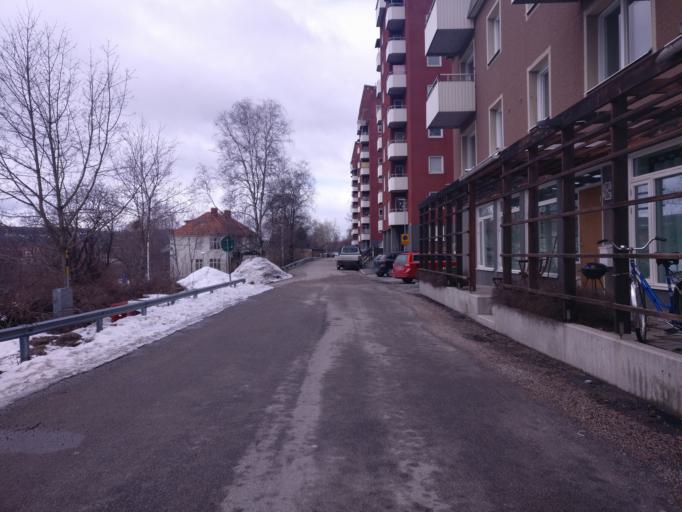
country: SE
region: Vaesternorrland
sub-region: Sundsvalls Kommun
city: Sundsvall
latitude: 62.3952
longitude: 17.2970
